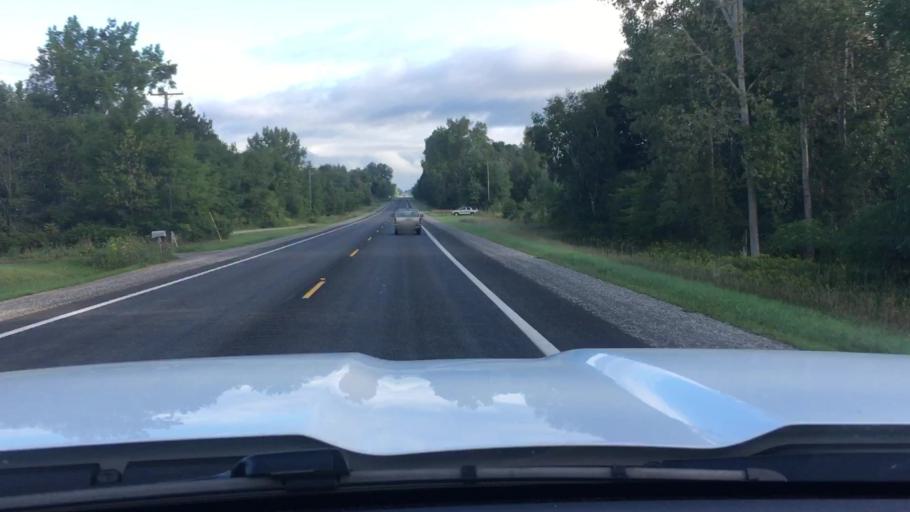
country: US
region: Michigan
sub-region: Tuscola County
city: Caro
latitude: 43.3585
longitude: -83.3828
